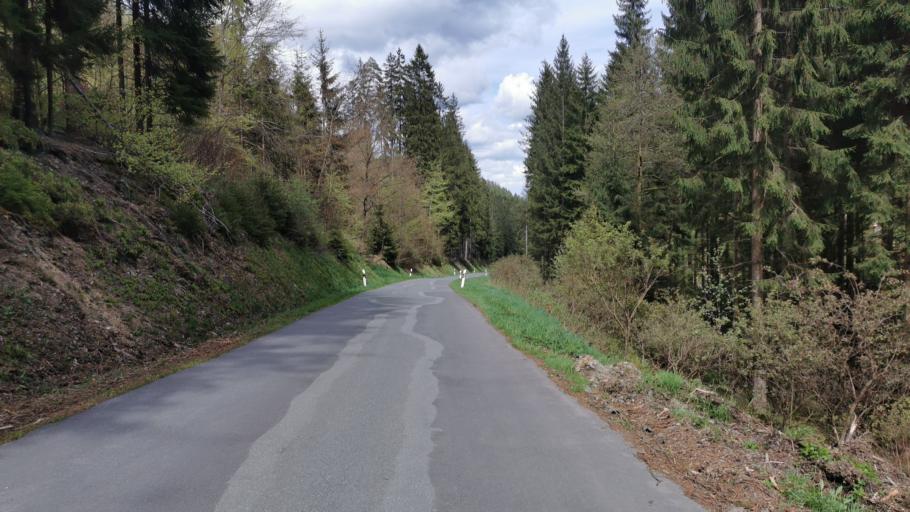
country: DE
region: Bavaria
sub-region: Upper Franconia
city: Ludwigsstadt
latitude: 50.4727
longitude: 11.3563
